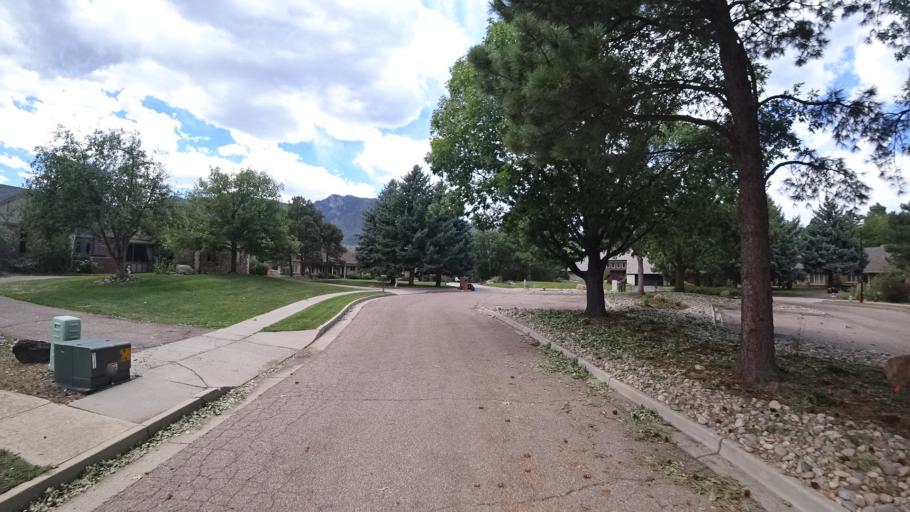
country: US
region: Colorado
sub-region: El Paso County
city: Colorado Springs
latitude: 38.7856
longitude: -104.8280
